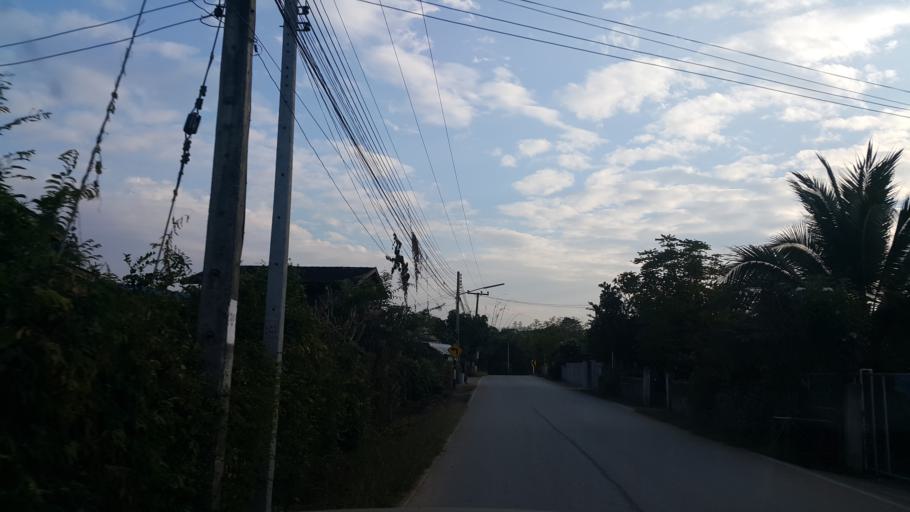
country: TH
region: Lampang
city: Sop Prap
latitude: 17.9026
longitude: 99.3288
